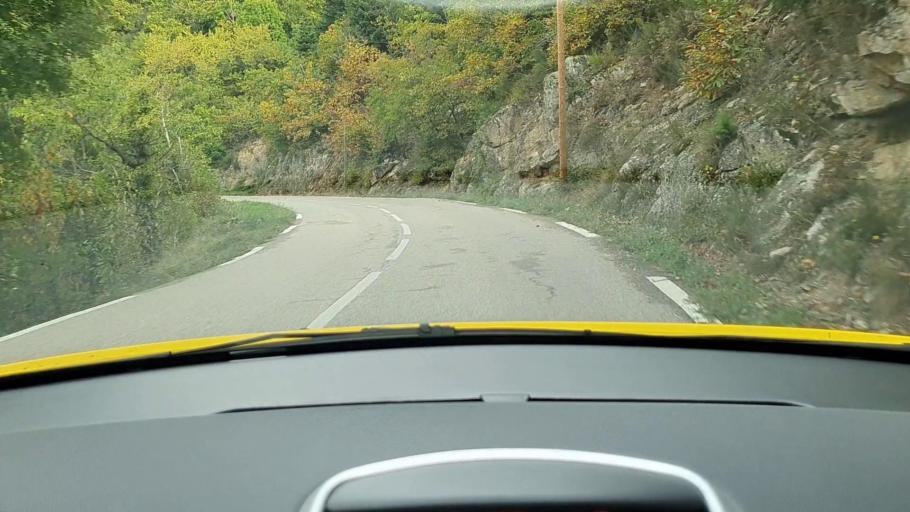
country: FR
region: Languedoc-Roussillon
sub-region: Departement du Gard
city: Le Vigan
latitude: 44.0246
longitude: 3.5980
